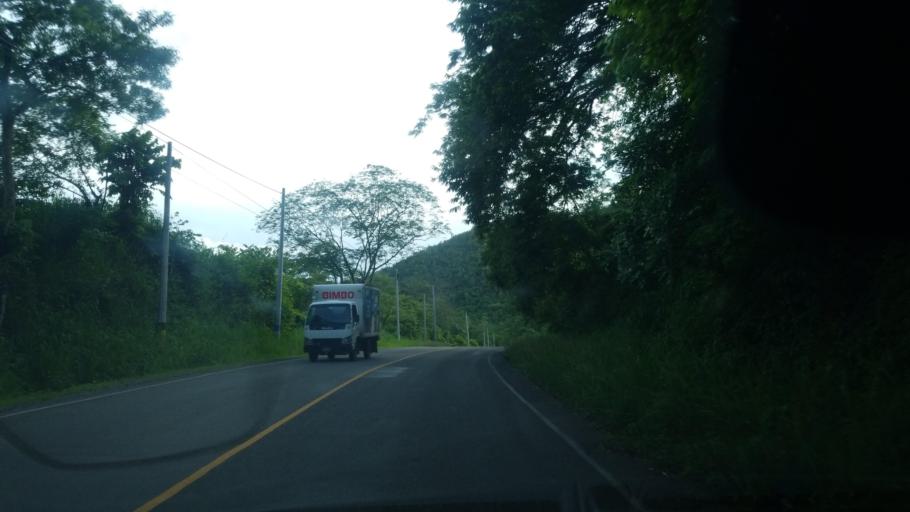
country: HN
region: Santa Barbara
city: Ilama
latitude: 15.1004
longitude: -88.2012
